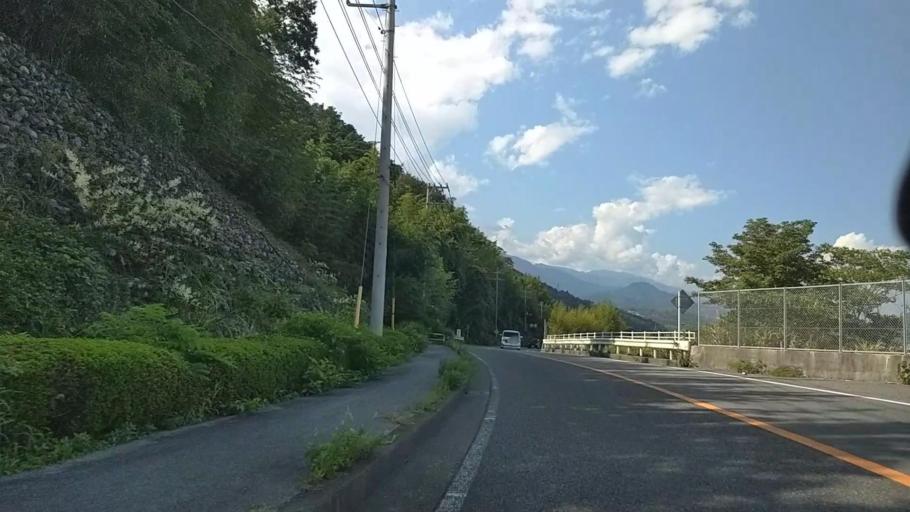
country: JP
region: Shizuoka
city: Fujinomiya
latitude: 35.3878
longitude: 138.4464
